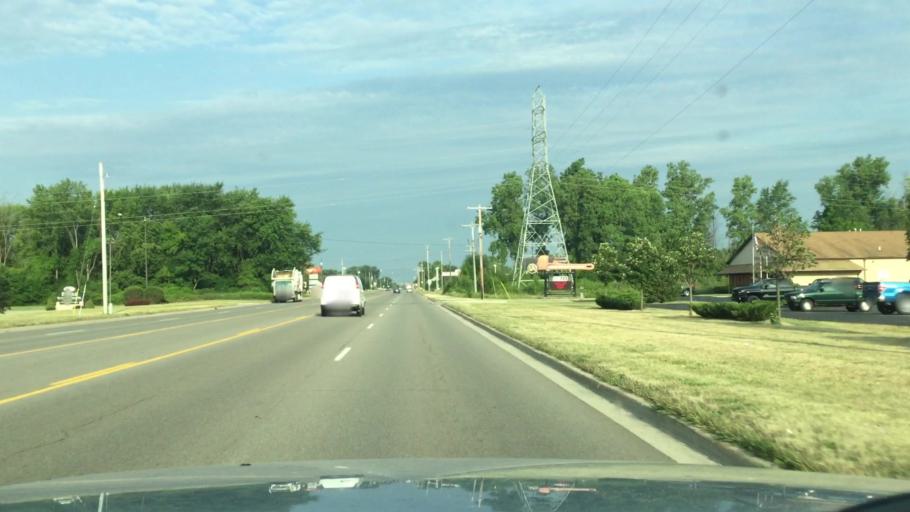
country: US
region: Michigan
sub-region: Genesee County
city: Flushing
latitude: 43.0604
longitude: -83.7905
